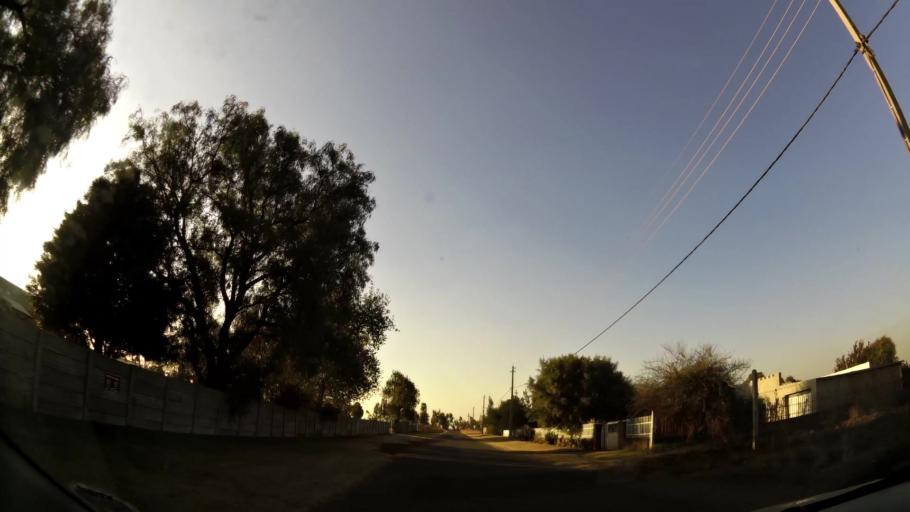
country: ZA
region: Gauteng
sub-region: West Rand District Municipality
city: Randfontein
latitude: -26.2042
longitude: 27.6448
